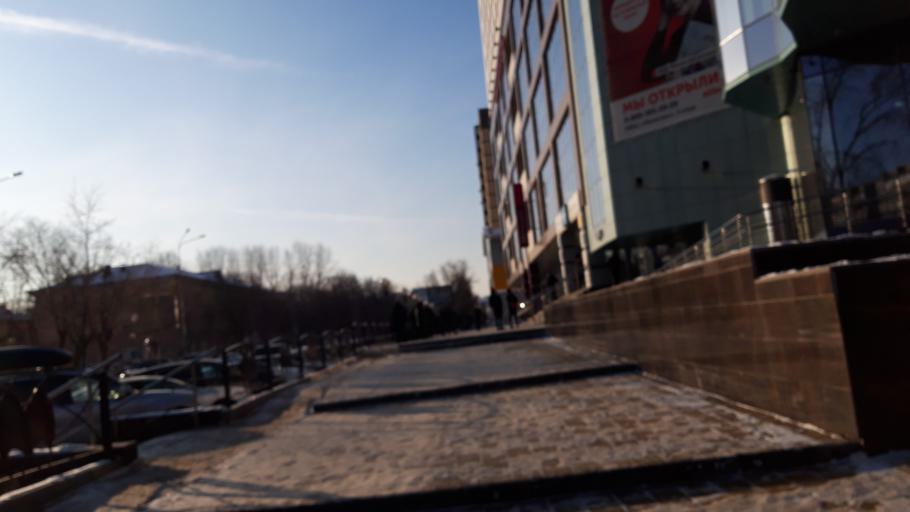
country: RU
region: Tjumen
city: Tyumen
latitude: 57.1522
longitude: 65.5678
